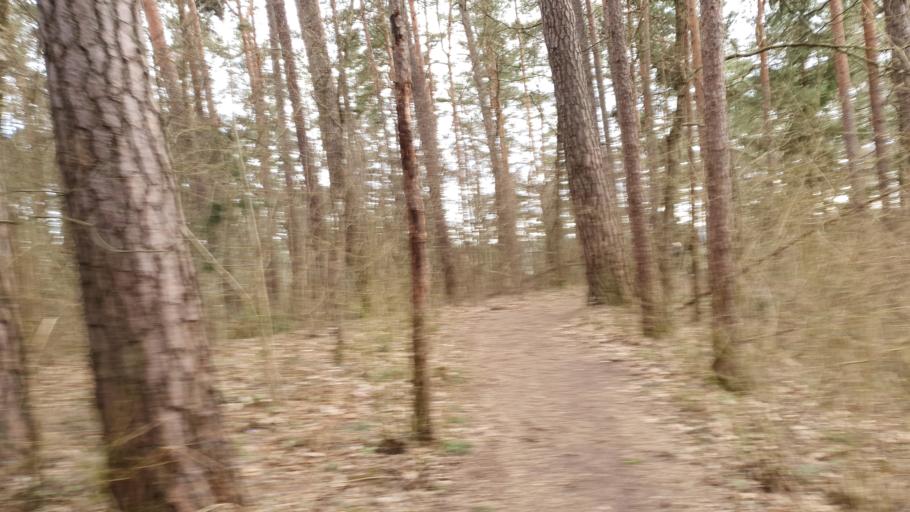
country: LT
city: Grigiskes
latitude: 54.7392
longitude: 25.0250
